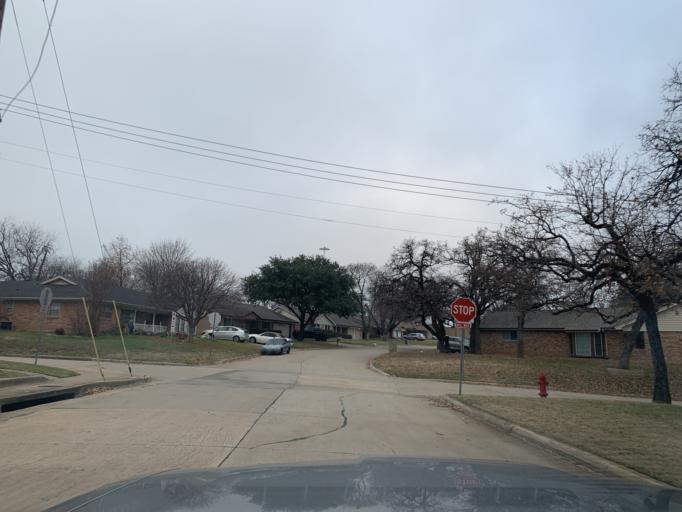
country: US
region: Texas
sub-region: Tarrant County
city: Bedford
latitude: 32.8379
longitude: -97.1575
